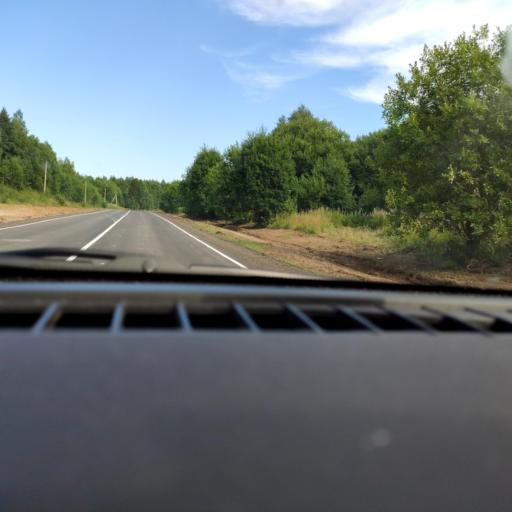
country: RU
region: Perm
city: Polazna
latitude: 58.3382
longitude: 56.1796
